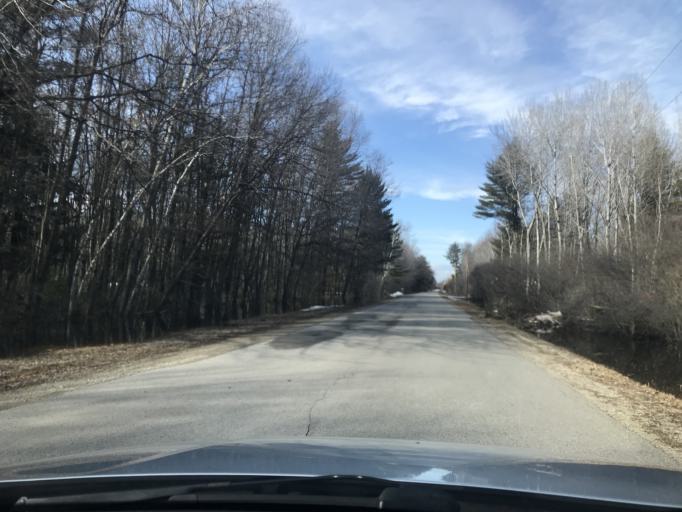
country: US
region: Wisconsin
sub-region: Marinette County
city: Marinette
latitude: 45.0326
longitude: -87.6676
